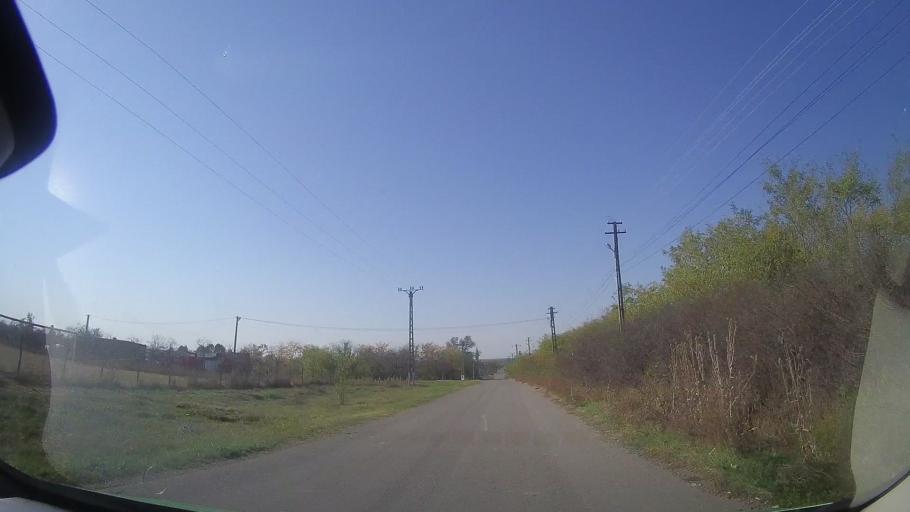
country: RO
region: Timis
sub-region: Comuna Ghizela
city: Ghizela
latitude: 45.8248
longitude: 21.7517
